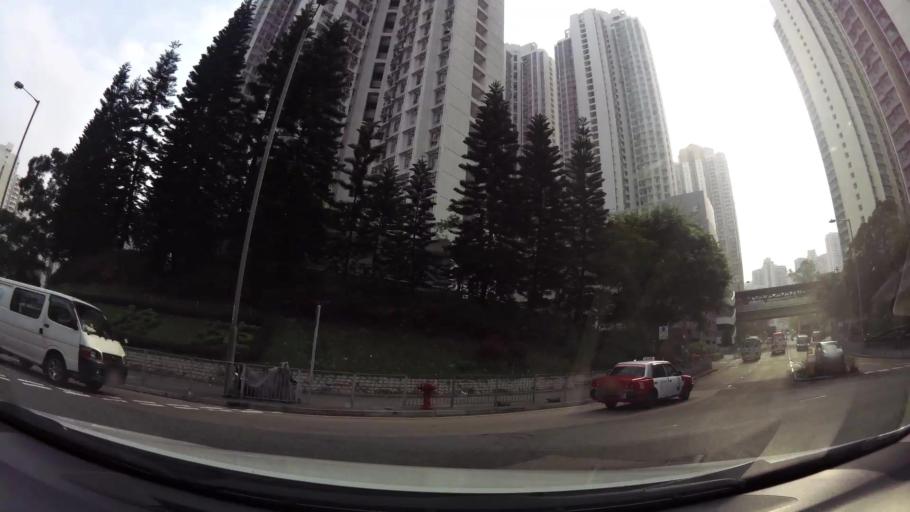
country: HK
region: Kowloon City
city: Kowloon
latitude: 22.3101
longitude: 114.2338
